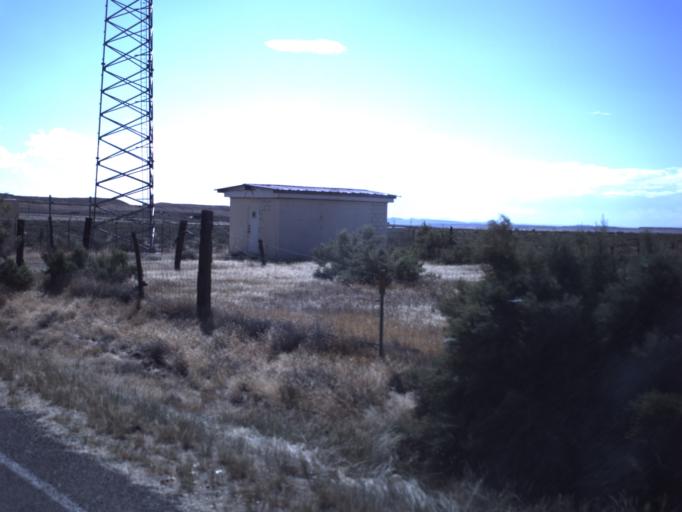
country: US
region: Utah
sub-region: Grand County
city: Moab
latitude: 38.9696
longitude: -109.7151
